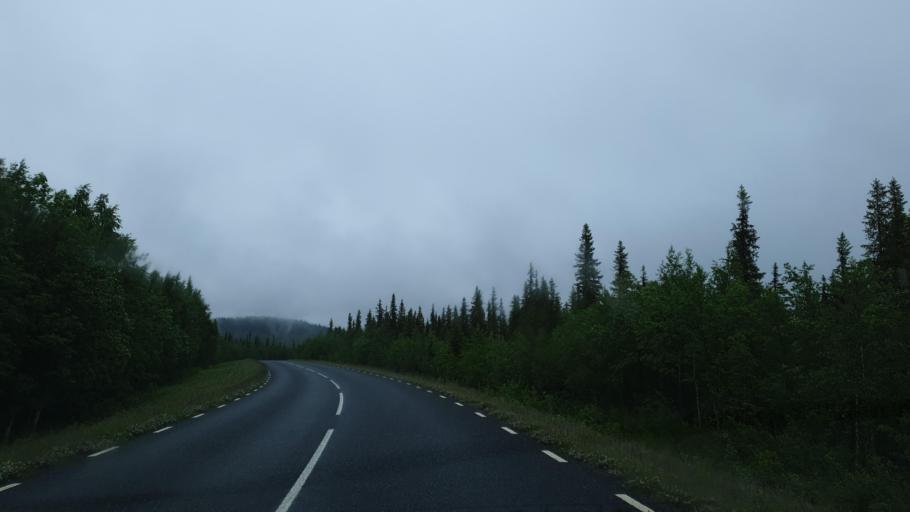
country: SE
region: Vaesterbotten
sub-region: Vilhelmina Kommun
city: Sjoberg
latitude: 65.2530
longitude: 15.6423
